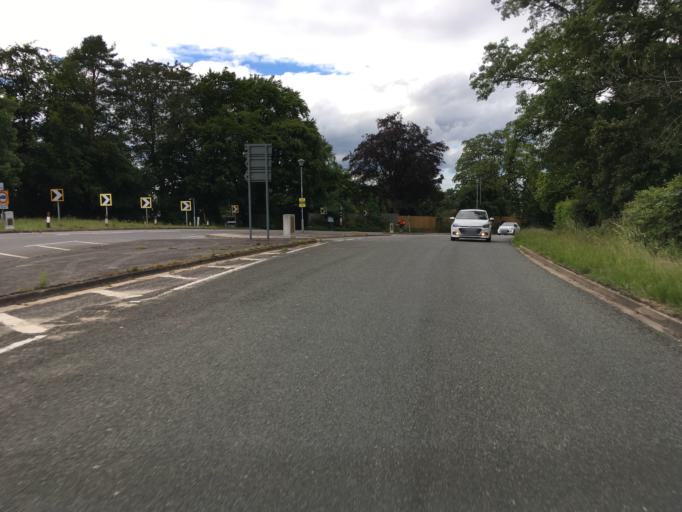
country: GB
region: England
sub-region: Oxfordshire
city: Boars Hill
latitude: 51.7221
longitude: -1.2681
